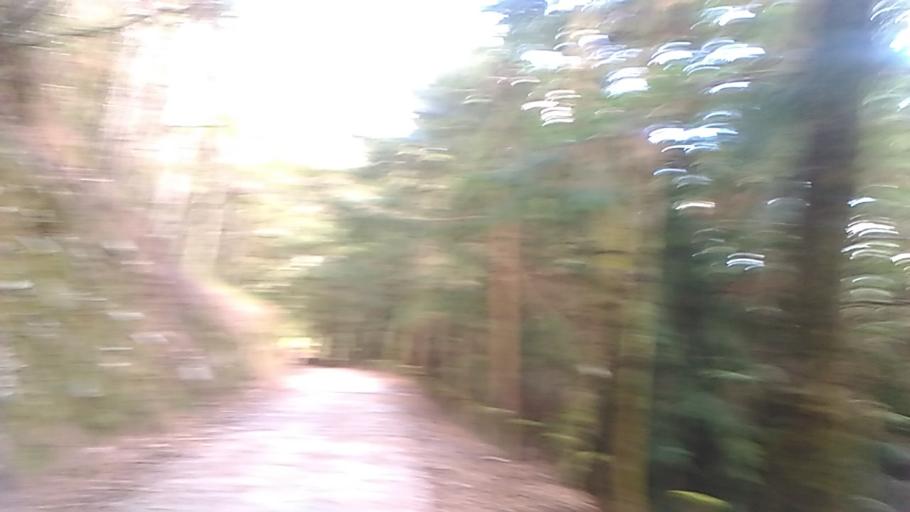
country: TW
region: Taiwan
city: Daxi
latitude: 24.4052
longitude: 121.3049
